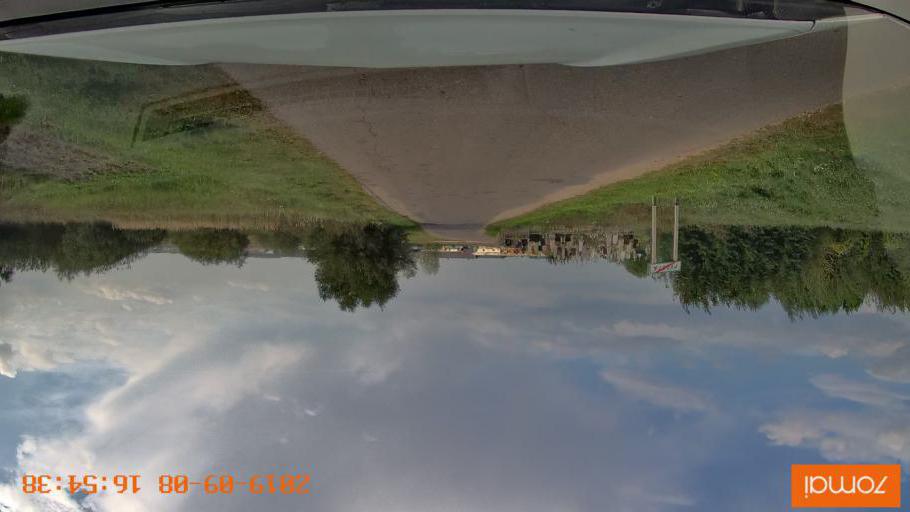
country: BY
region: Grodnenskaya
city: Hrodna
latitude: 53.7503
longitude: 23.9208
